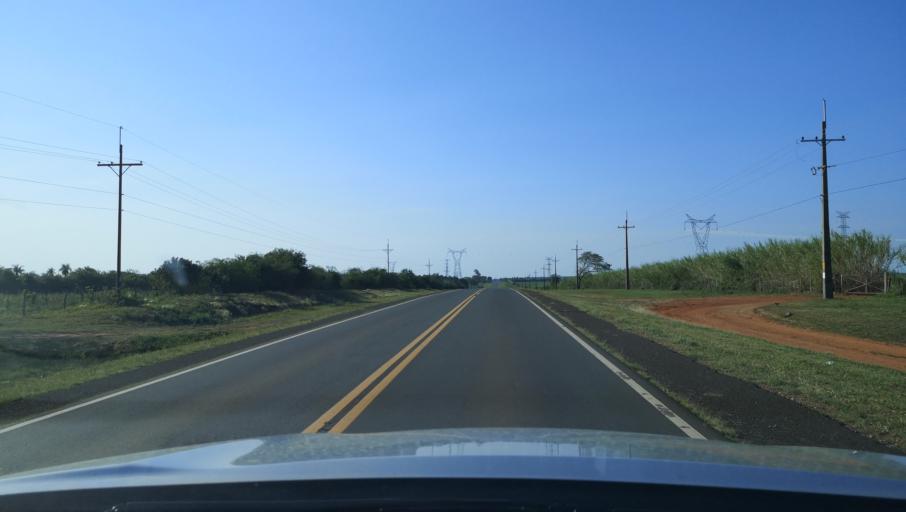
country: PY
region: Misiones
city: Santa Maria
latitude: -26.7962
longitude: -57.0230
